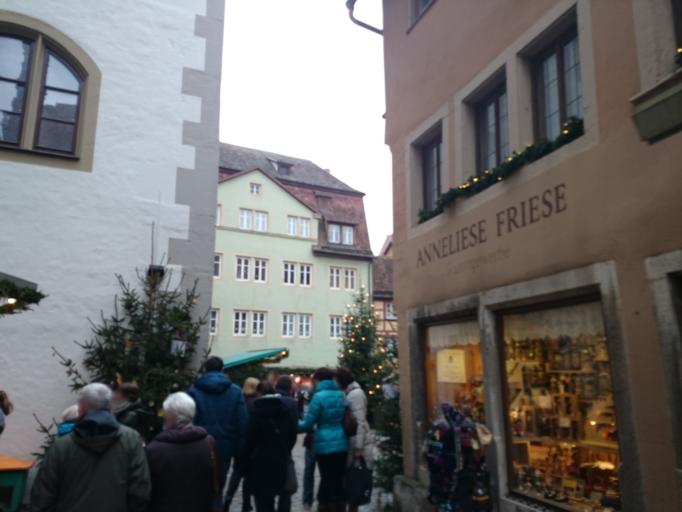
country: DE
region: Bavaria
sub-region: Regierungsbezirk Mittelfranken
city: Rothenburg ob der Tauber
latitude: 49.3774
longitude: 10.1787
